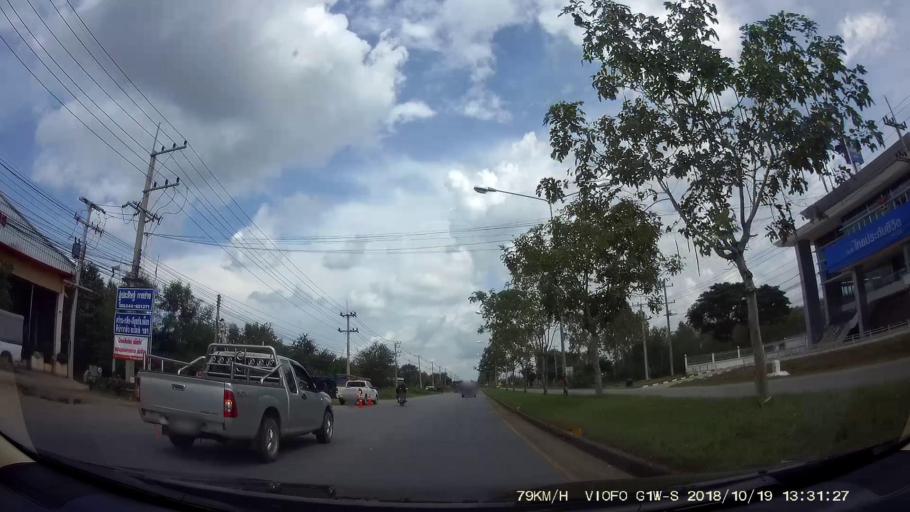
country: TH
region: Chaiyaphum
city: Chatturat
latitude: 15.5772
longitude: 101.8676
